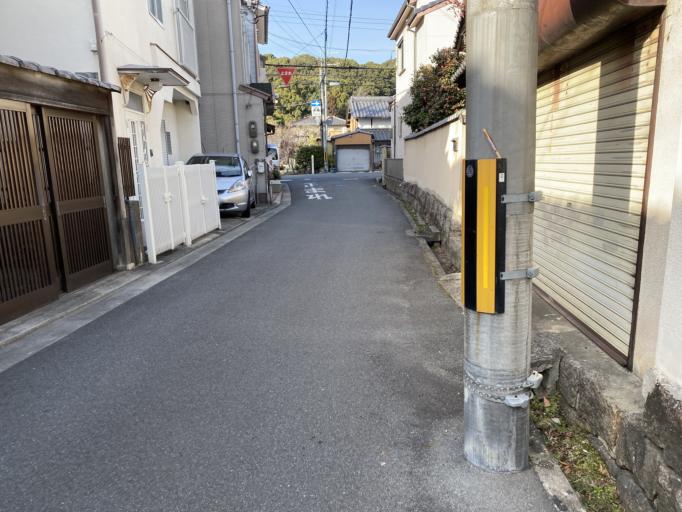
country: JP
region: Nara
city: Nara-shi
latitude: 34.6913
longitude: 135.8299
